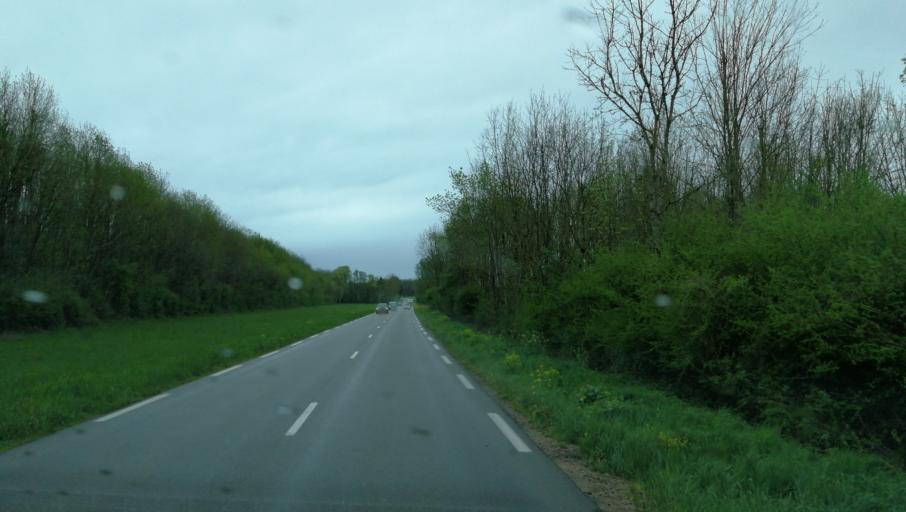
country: FR
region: Franche-Comte
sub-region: Departement du Jura
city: Bletterans
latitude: 46.7230
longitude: 5.4732
